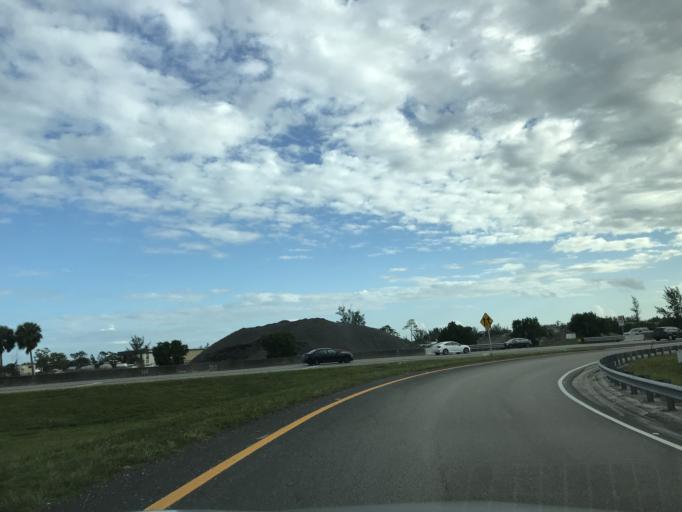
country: US
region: Florida
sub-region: Palm Beach County
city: Lake Belvedere Estates
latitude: 26.6850
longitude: -80.1632
